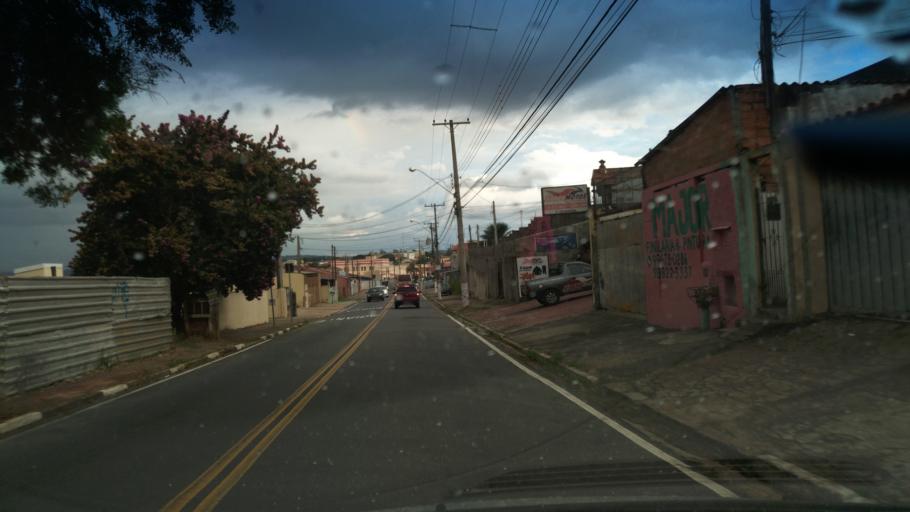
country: BR
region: Sao Paulo
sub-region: Campinas
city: Campinas
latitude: -22.9318
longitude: -47.0330
